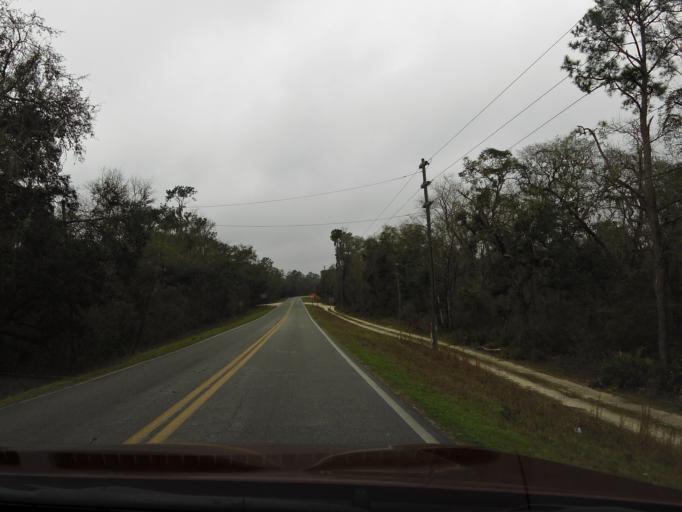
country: US
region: Florida
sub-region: Gilchrist County
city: Trenton
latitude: 29.7958
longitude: -82.9211
